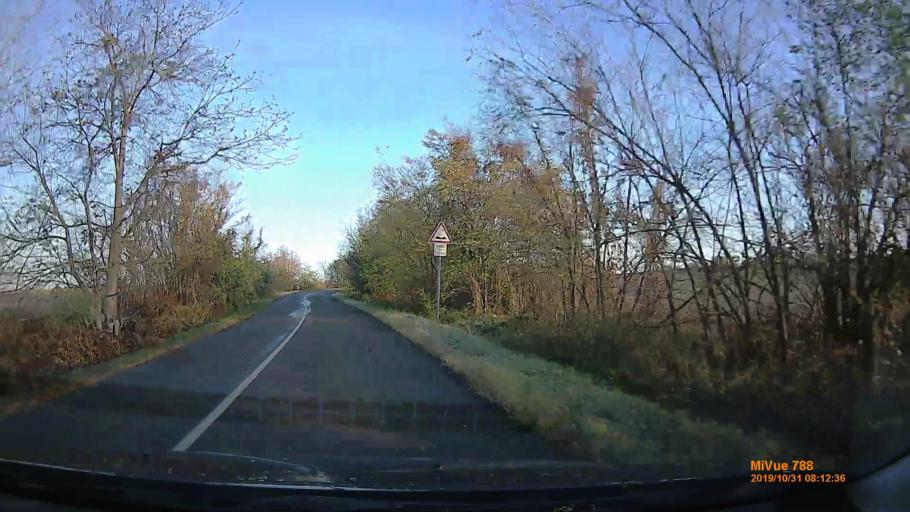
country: HU
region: Pest
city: Pilis
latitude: 47.3270
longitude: 19.5673
